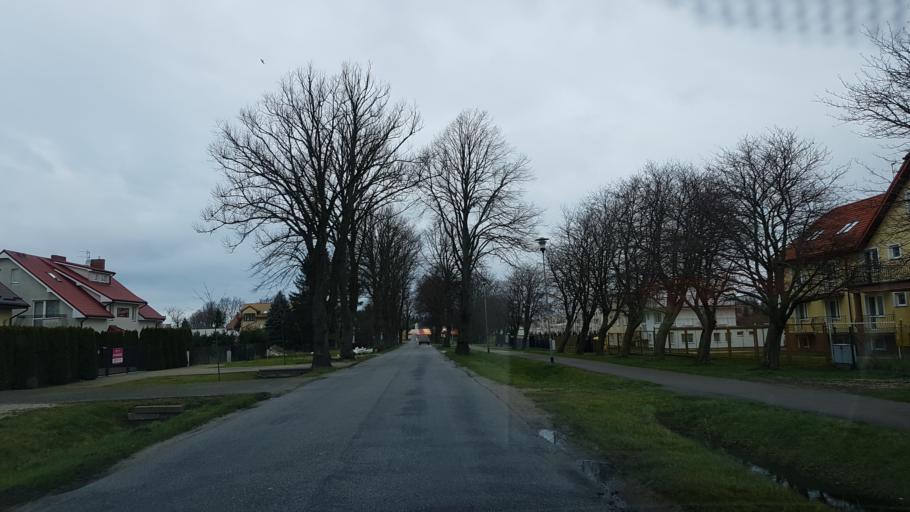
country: PL
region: West Pomeranian Voivodeship
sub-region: Powiat kolobrzeski
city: Ustronie Morskie
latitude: 54.2095
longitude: 15.7465
